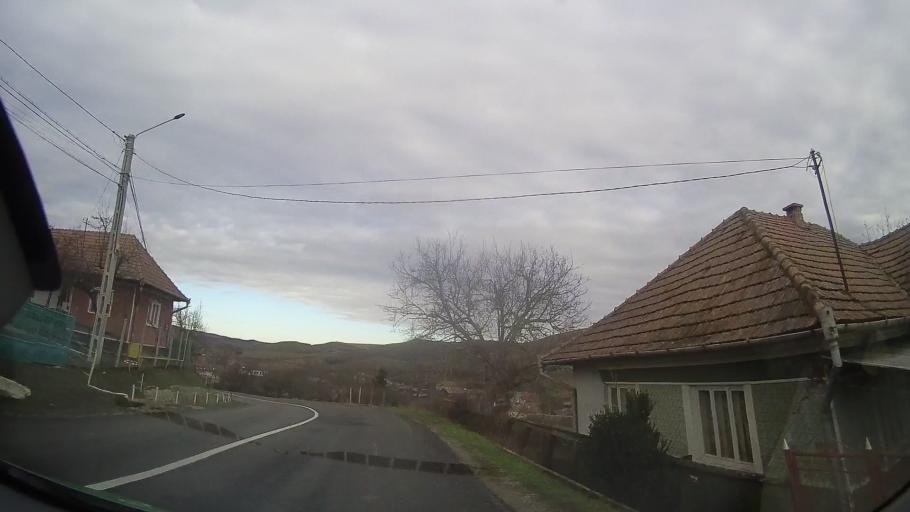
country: RO
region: Bistrita-Nasaud
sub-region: Comuna Micestii de Campie
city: Micestii de Campie
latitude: 46.8569
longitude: 24.3111
